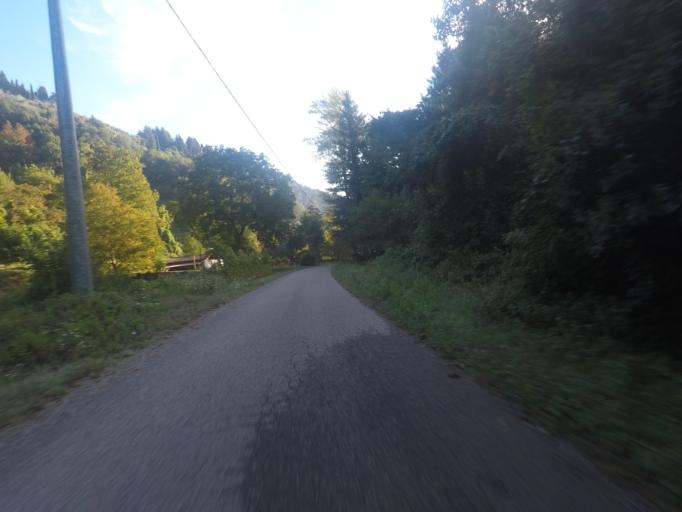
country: IT
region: Tuscany
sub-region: Provincia di Lucca
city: Pescaglia
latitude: 43.9514
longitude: 10.4184
